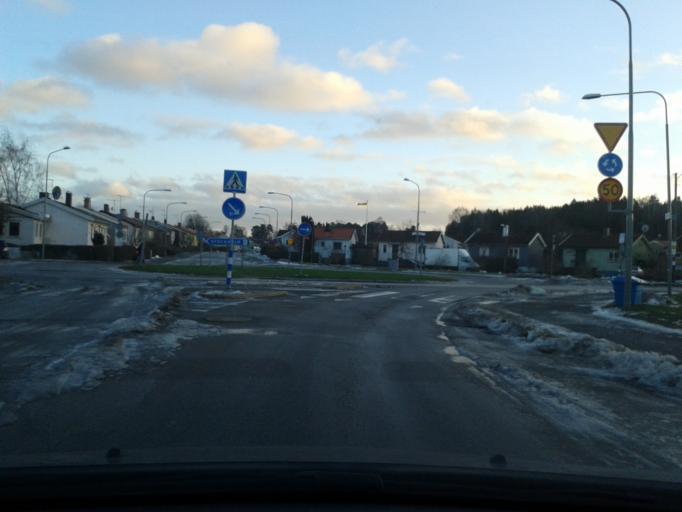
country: SE
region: Stockholm
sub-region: Stockholms Kommun
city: Arsta
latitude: 59.2695
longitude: 18.0882
